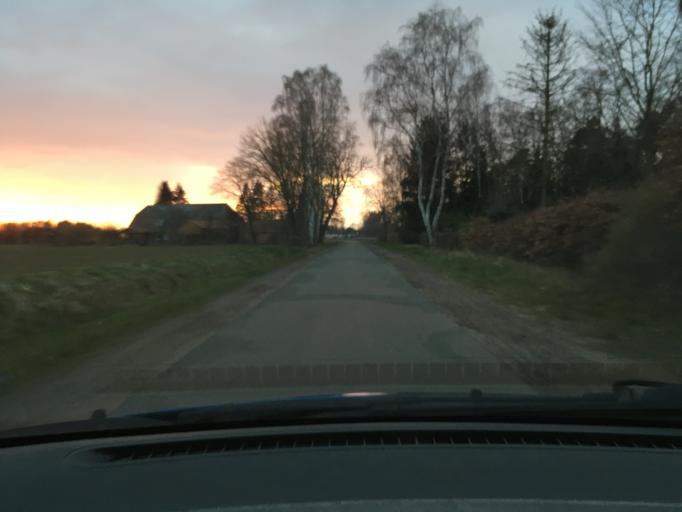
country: DE
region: Lower Saxony
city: Bleckede
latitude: 53.2974
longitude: 10.6788
